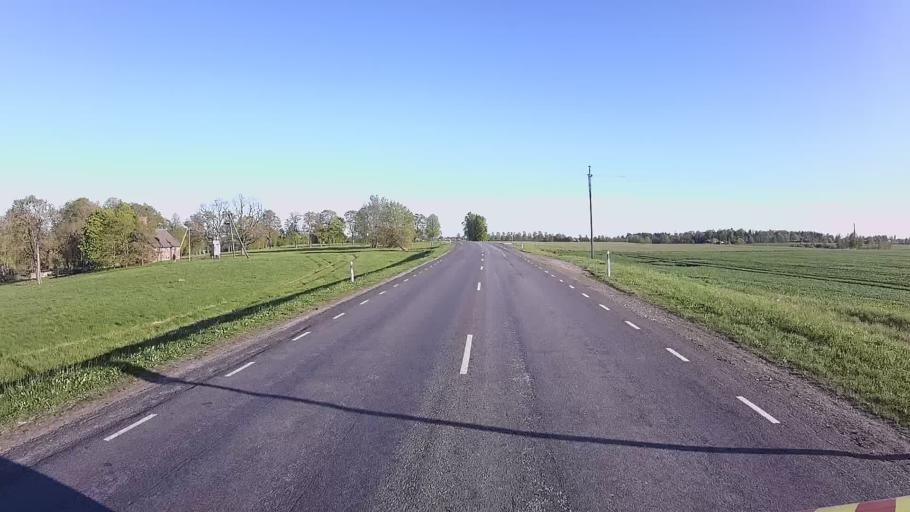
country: EE
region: Viljandimaa
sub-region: Viljandi linn
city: Viljandi
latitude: 58.3977
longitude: 25.5918
